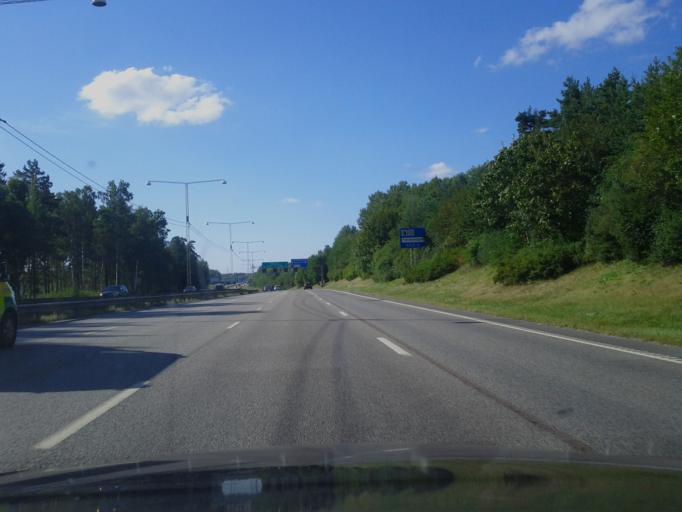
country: SE
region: Stockholm
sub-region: Stockholms Kommun
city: Kista
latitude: 59.4097
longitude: 17.9554
